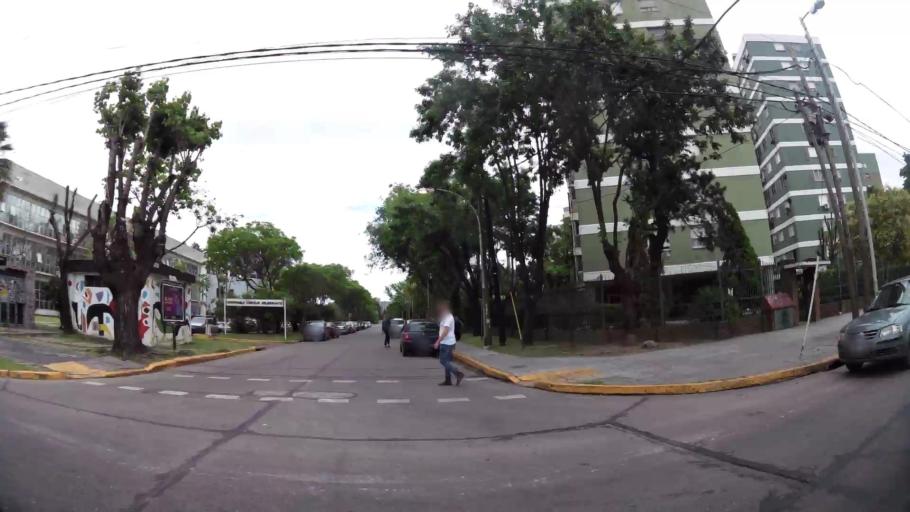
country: AR
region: Buenos Aires
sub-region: Partido de Avellaneda
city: Avellaneda
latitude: -34.6746
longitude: -58.3637
